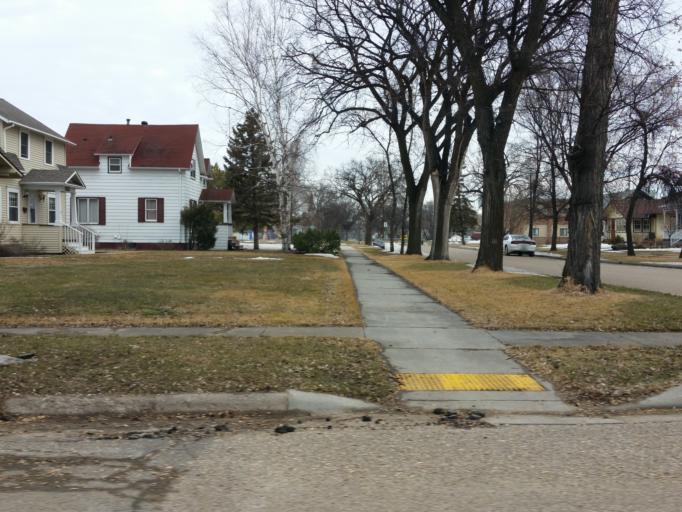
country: US
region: North Dakota
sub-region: Walsh County
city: Grafton
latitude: 48.4155
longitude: -97.4144
